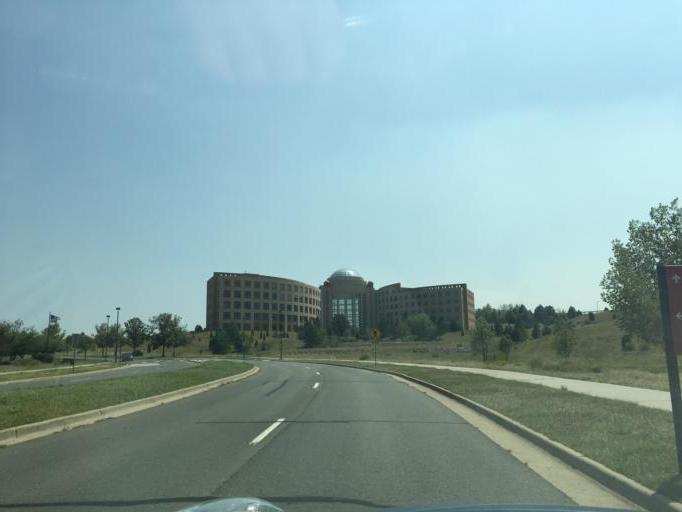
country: US
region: Colorado
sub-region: Jefferson County
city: West Pleasant View
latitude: 39.7303
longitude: -105.2049
